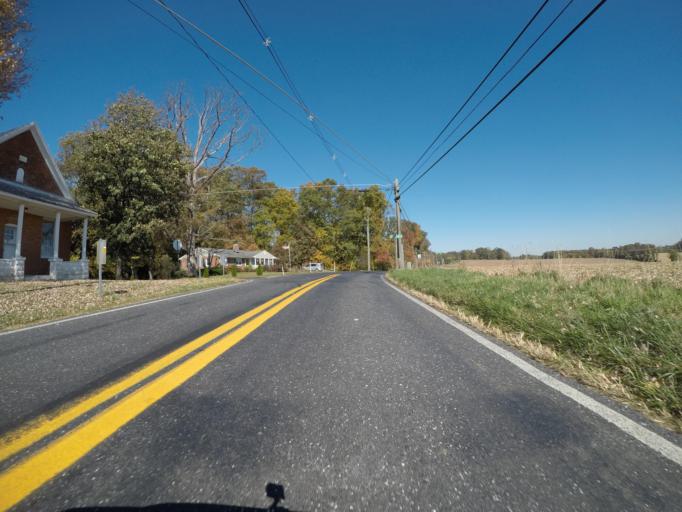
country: US
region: Maryland
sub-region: Carroll County
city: Hampstead
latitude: 39.5727
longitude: -76.8794
